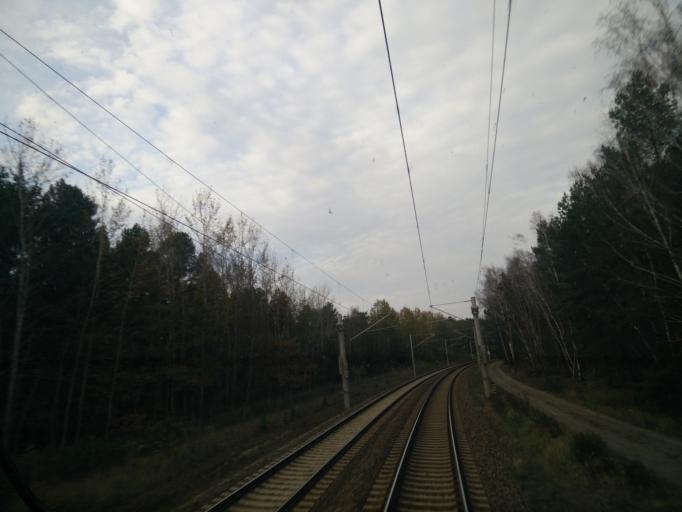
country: DE
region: Brandenburg
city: Bestensee
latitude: 52.2126
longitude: 13.6179
